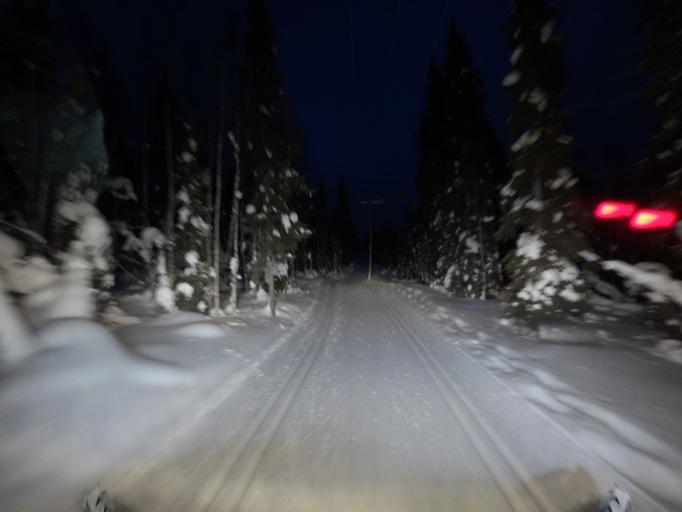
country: FI
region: Lapland
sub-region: Tunturi-Lappi
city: Kolari
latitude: 67.5860
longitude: 24.0869
